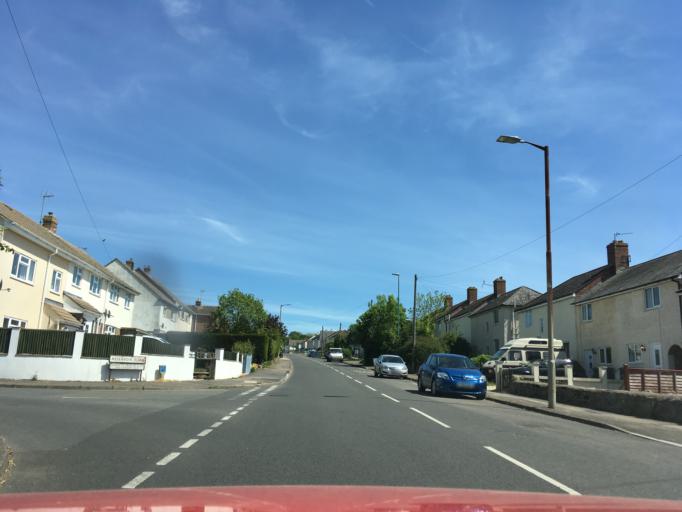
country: GB
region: England
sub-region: Gloucestershire
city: Stroud
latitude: 51.7446
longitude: -2.1986
